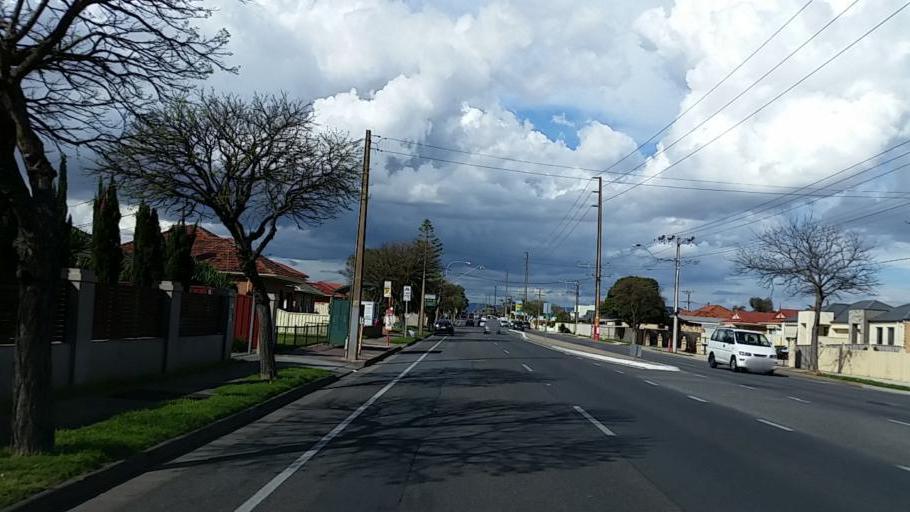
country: AU
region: South Australia
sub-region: Charles Sturt
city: Seaton
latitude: -34.9065
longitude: 138.5105
